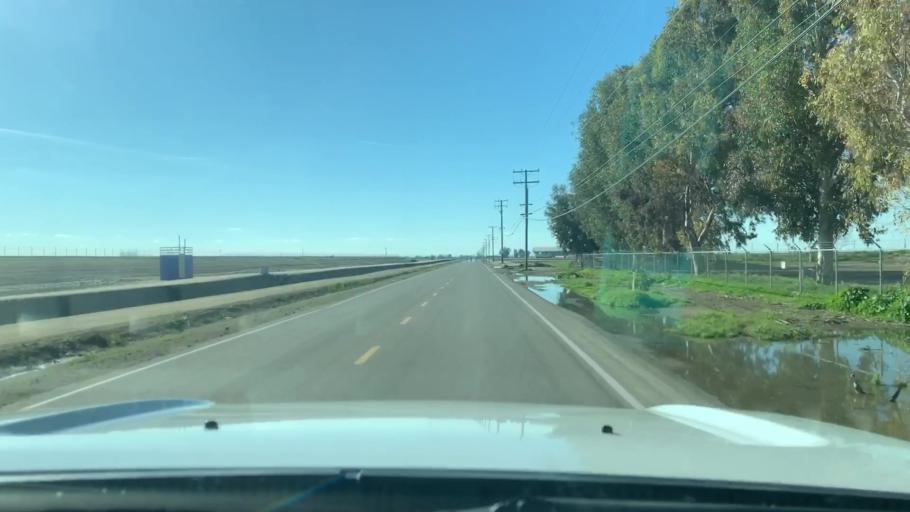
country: US
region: California
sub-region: Tulare County
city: Tulare
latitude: 36.1819
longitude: -119.3766
